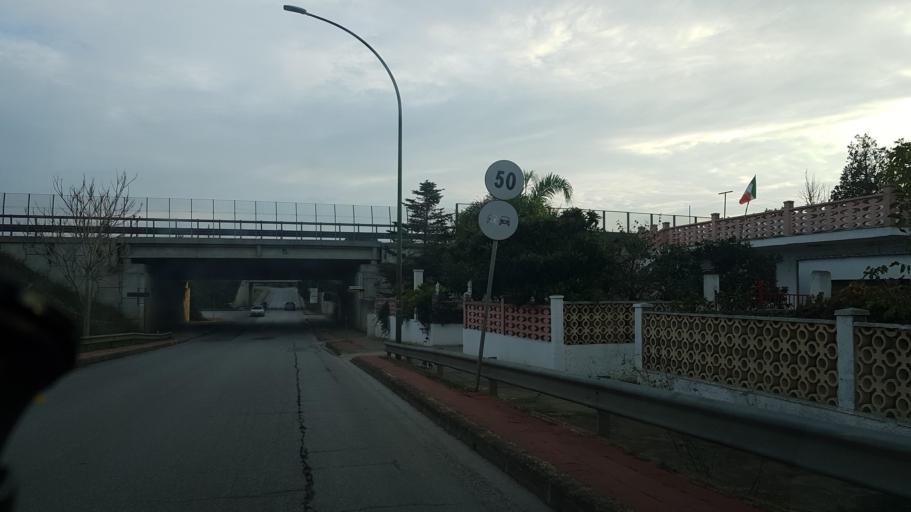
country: IT
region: Apulia
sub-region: Provincia di Brindisi
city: Latiano
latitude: 40.5591
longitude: 17.7152
